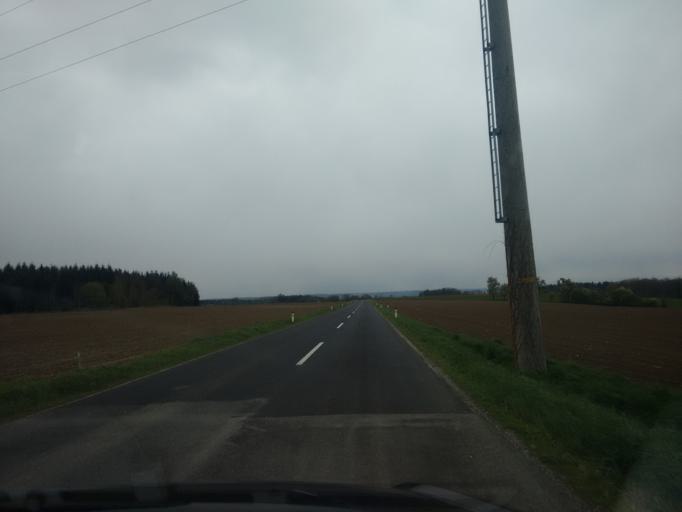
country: AT
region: Upper Austria
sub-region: Wels-Land
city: Holzhausen
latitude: 48.2324
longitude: 14.0692
